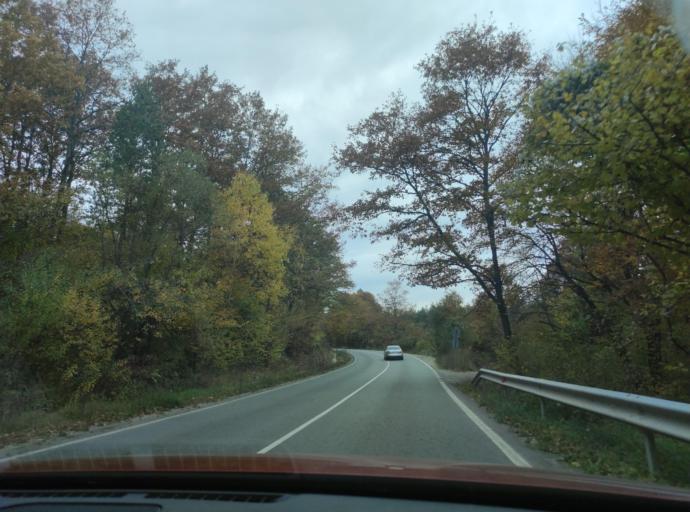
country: BG
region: Sofiya
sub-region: Obshtina Godech
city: Godech
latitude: 42.9803
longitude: 23.1347
